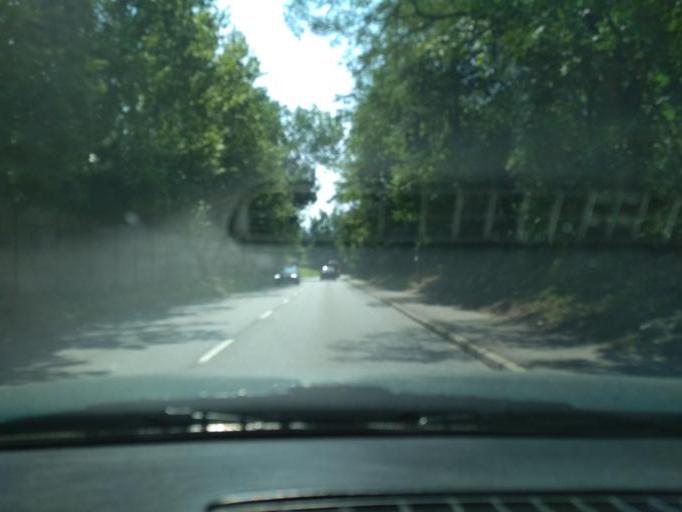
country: PL
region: Silesian Voivodeship
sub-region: Katowice
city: Katowice
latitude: 50.2831
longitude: 19.0068
